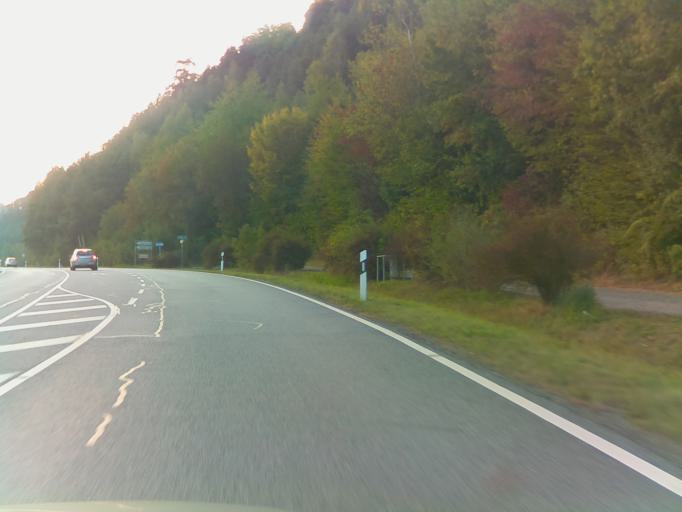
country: DE
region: Hesse
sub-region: Regierungsbezirk Darmstadt
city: Beerfelden
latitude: 49.6097
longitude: 8.9780
